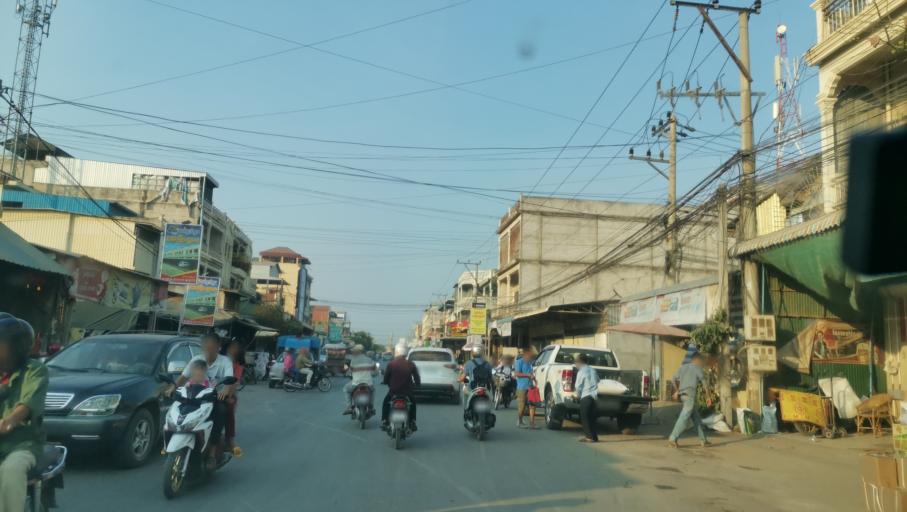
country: KH
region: Battambang
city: Battambang
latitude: 13.1045
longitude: 103.1927
